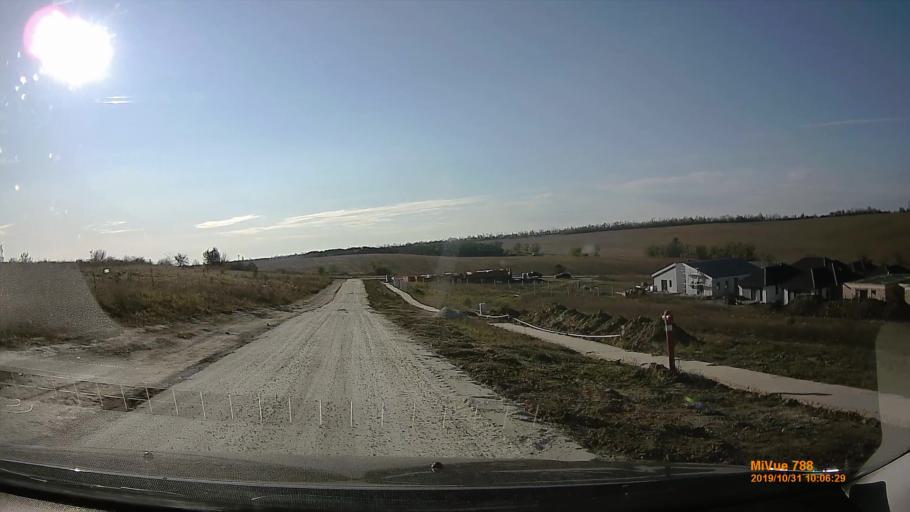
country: HU
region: Pest
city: Pecel
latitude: 47.4691
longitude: 19.3472
